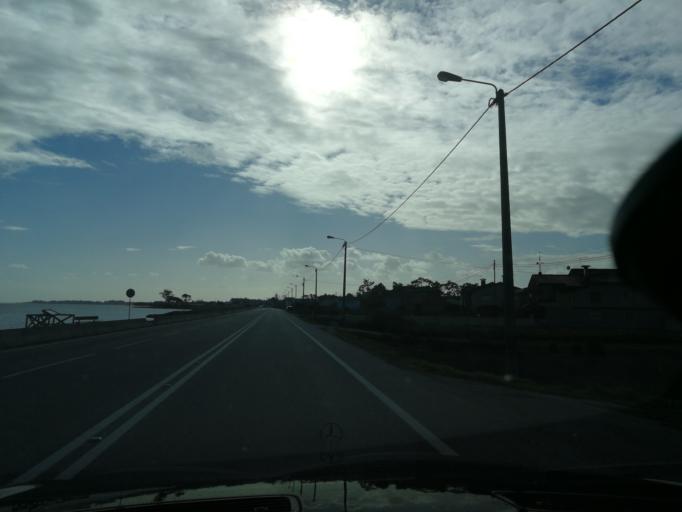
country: PT
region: Aveiro
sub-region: Estarreja
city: Pardilho
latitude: 40.7795
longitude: -8.6902
